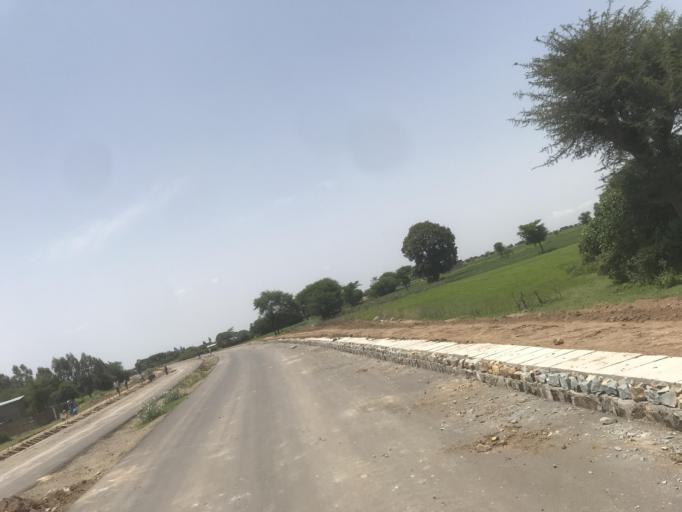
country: ET
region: Oromiya
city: Mojo
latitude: 8.2980
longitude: 38.9399
